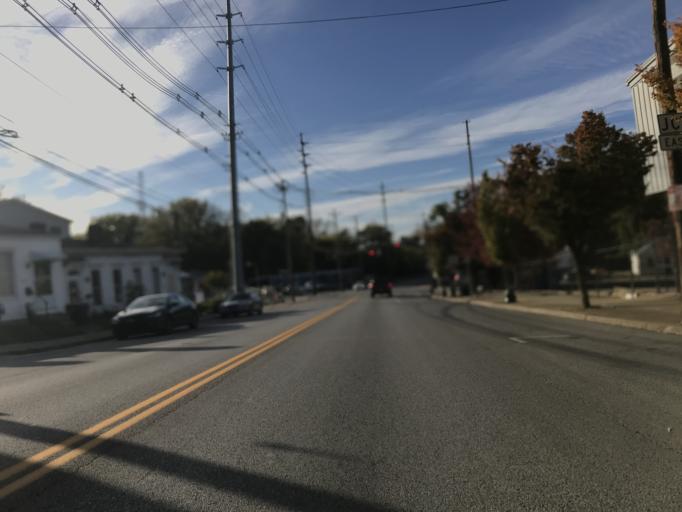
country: US
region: Indiana
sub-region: Clark County
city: Jeffersonville
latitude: 38.2575
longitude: -85.7187
